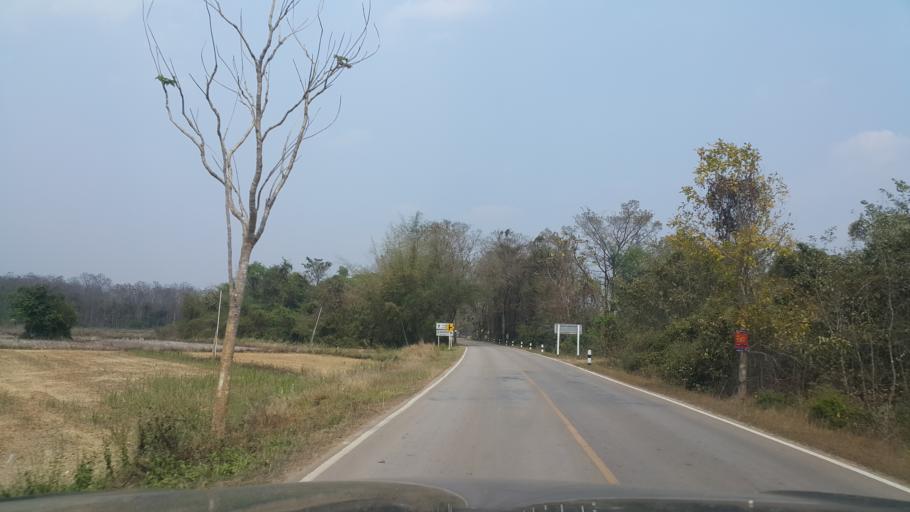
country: TH
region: Lampang
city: Soem Ngam
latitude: 18.0173
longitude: 99.2203
